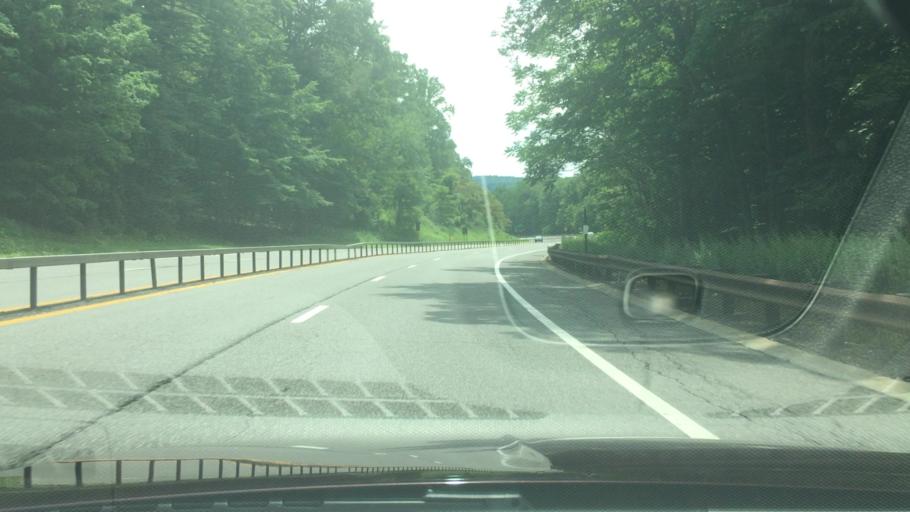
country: US
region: New York
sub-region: Westchester County
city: Shrub Oak
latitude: 41.3415
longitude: -73.8132
